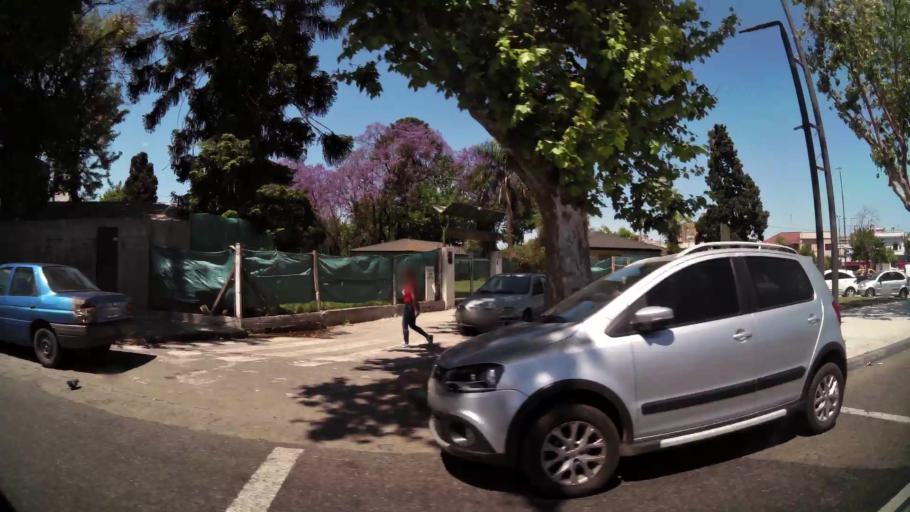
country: AR
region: Buenos Aires
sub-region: Partido de Avellaneda
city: Avellaneda
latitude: -34.6562
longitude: -58.4164
